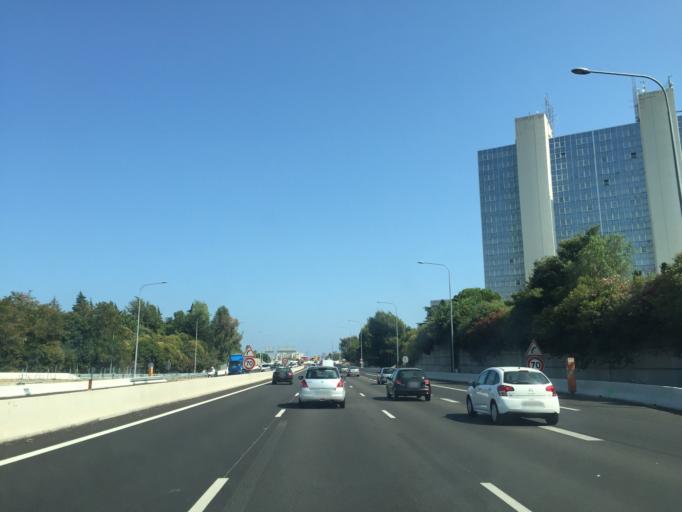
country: FR
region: Provence-Alpes-Cote d'Azur
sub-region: Departement des Alpes-Maritimes
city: Saint-Laurent-du-Var
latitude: 43.6745
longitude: 7.1977
